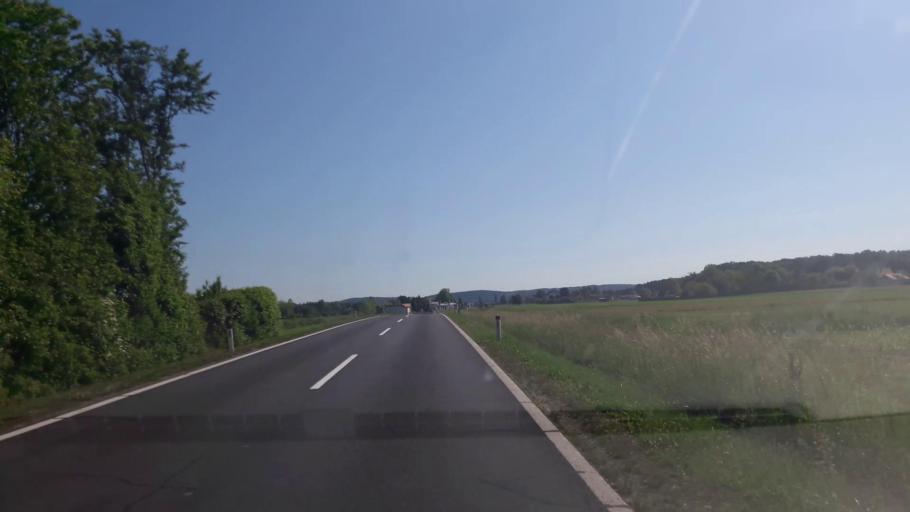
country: AT
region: Styria
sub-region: Politischer Bezirk Hartberg-Fuerstenfeld
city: Fuerstenfeld
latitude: 47.0295
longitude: 16.0816
